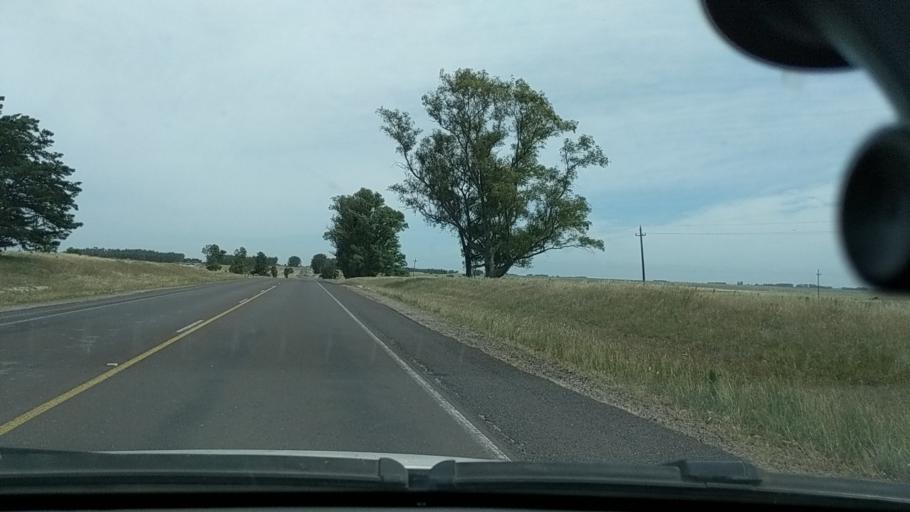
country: UY
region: Durazno
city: Durazno
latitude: -33.4721
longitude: -56.4529
